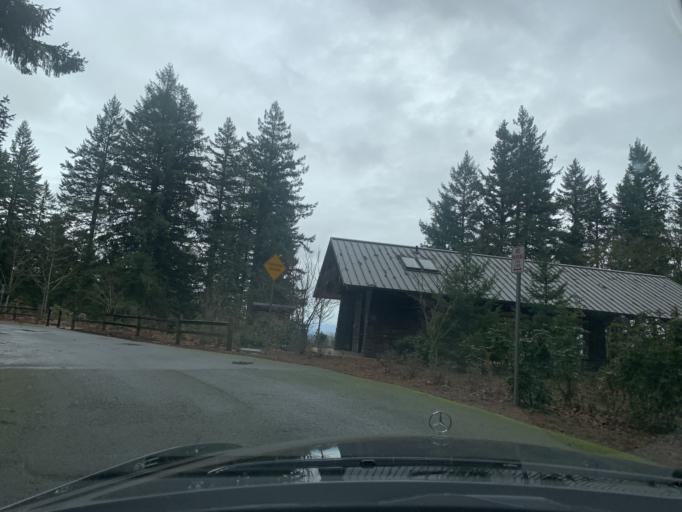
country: US
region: Oregon
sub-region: Clackamas County
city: Happy Valley
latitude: 45.4453
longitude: -122.5090
